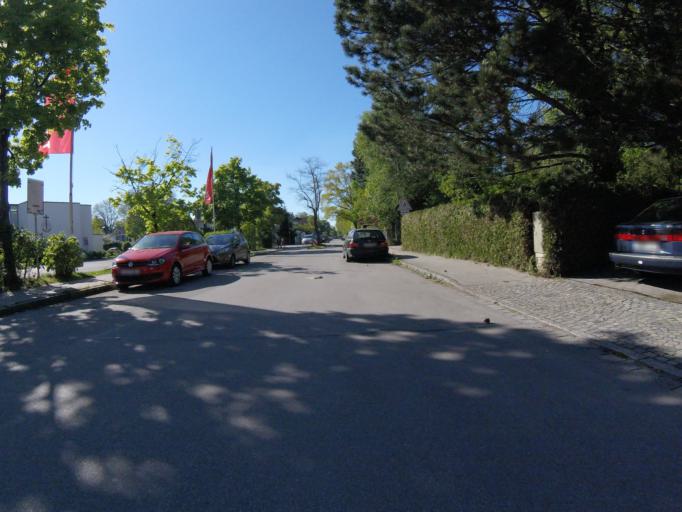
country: DE
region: Bavaria
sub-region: Upper Bavaria
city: Ottobrunn
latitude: 48.0633
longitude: 11.6770
